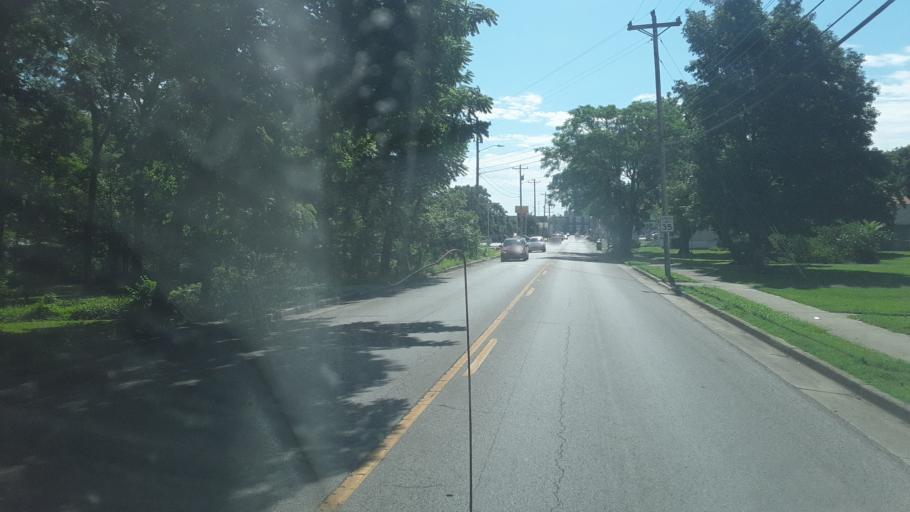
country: US
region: Kentucky
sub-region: Todd County
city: Elkton
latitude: 36.8105
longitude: -87.1586
